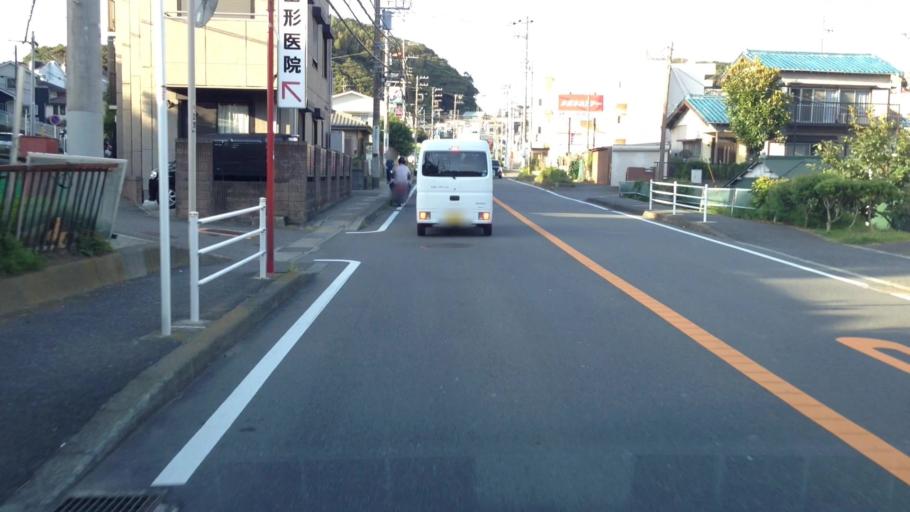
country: JP
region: Kanagawa
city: Yokosuka
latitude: 35.2284
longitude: 139.6516
